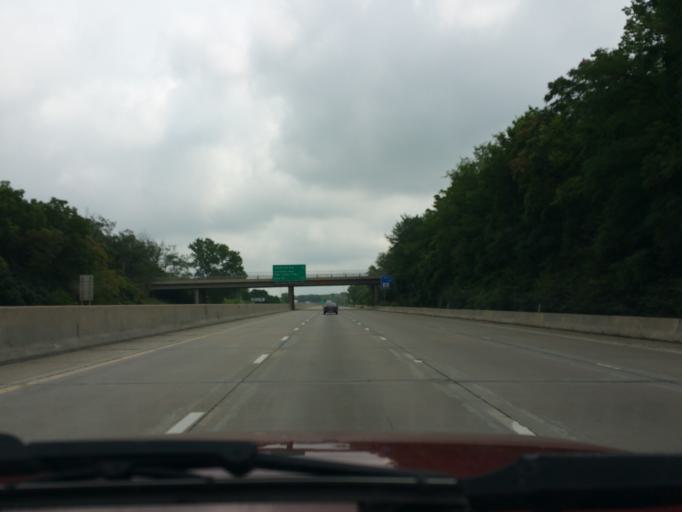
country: US
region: Kansas
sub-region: Shawnee County
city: Topeka
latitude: 39.0375
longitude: -95.6619
